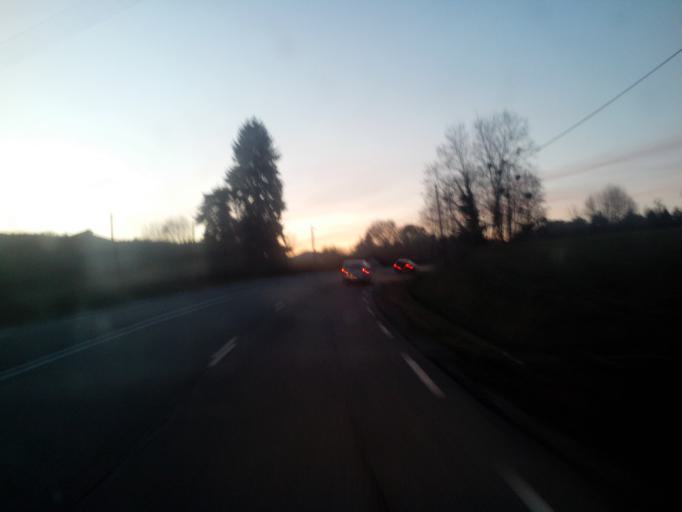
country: FR
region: Midi-Pyrenees
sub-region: Departement de l'Ariege
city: Foix
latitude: 42.9698
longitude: 1.5877
